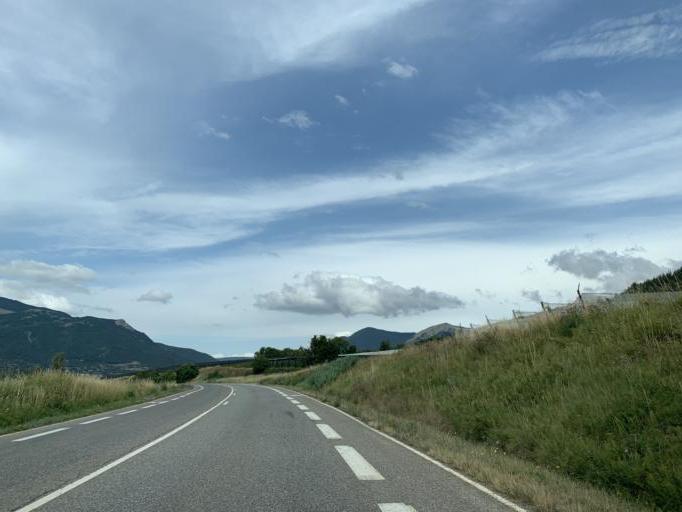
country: FR
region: Provence-Alpes-Cote d'Azur
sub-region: Departement des Hautes-Alpes
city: La Roche-des-Arnauds
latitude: 44.5463
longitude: 5.9995
